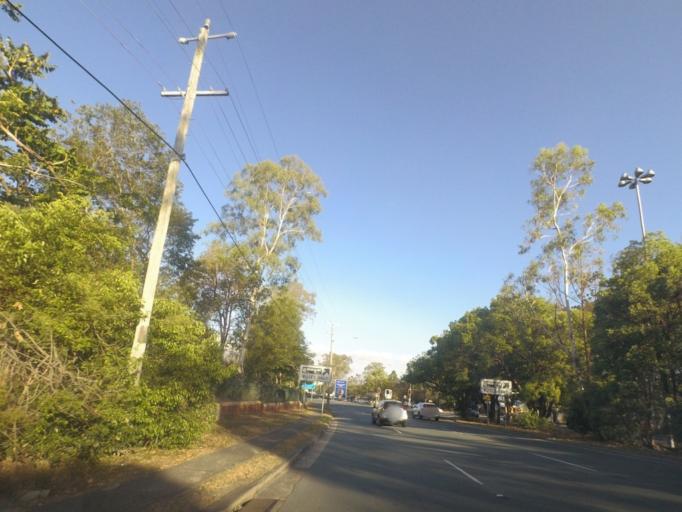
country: AU
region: Queensland
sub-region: Brisbane
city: Toowong
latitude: -27.4779
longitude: 152.9820
